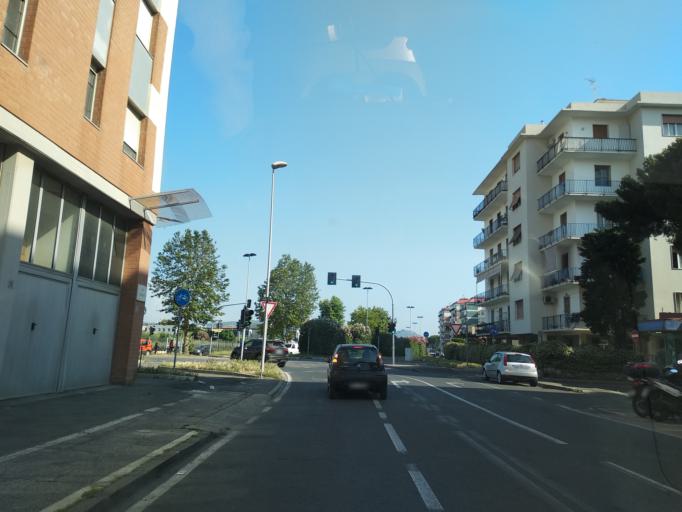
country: IT
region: Tuscany
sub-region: Provincia di Livorno
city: Livorno
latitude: 43.5383
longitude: 10.3222
